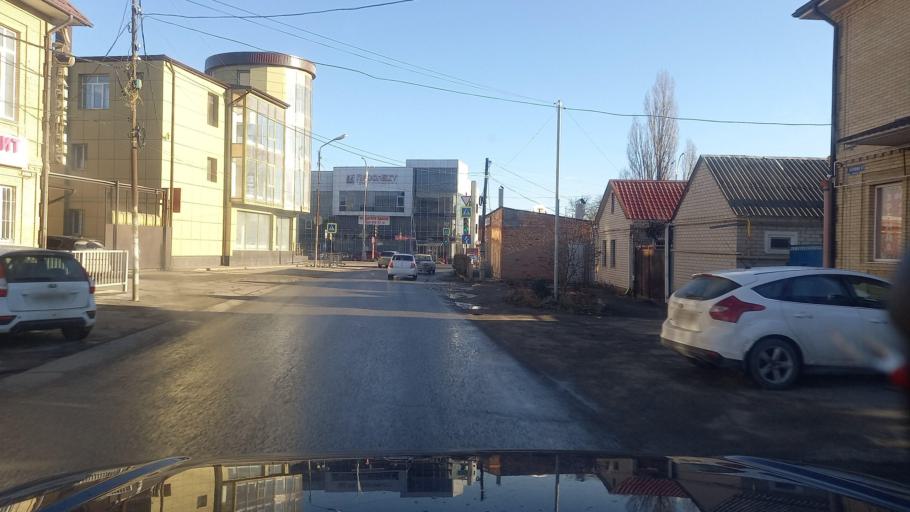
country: RU
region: Stavropol'skiy
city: Goryachevodskiy
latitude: 44.0269
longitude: 43.0728
